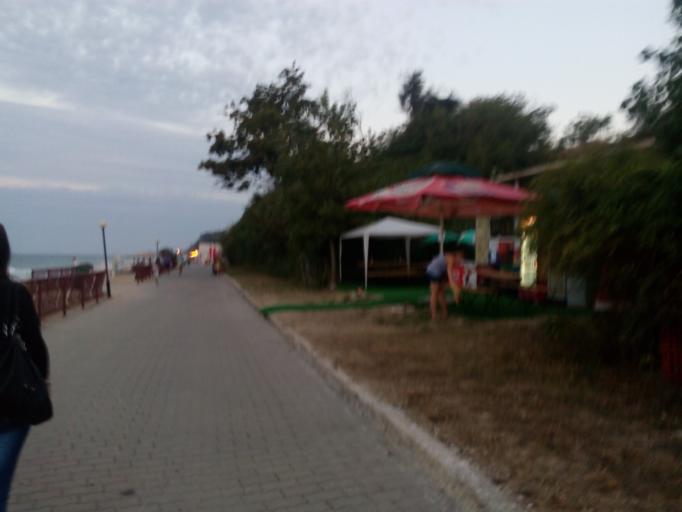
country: BG
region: Burgas
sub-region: Obshtina Nesebur
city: Obzor
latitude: 42.8169
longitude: 27.8854
